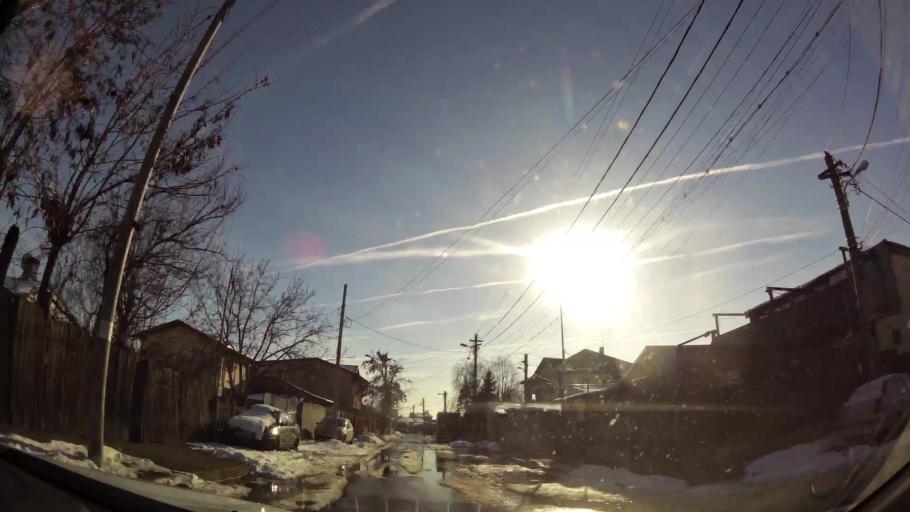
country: RO
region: Ilfov
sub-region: Voluntari City
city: Voluntari
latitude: 44.4832
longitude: 26.1428
